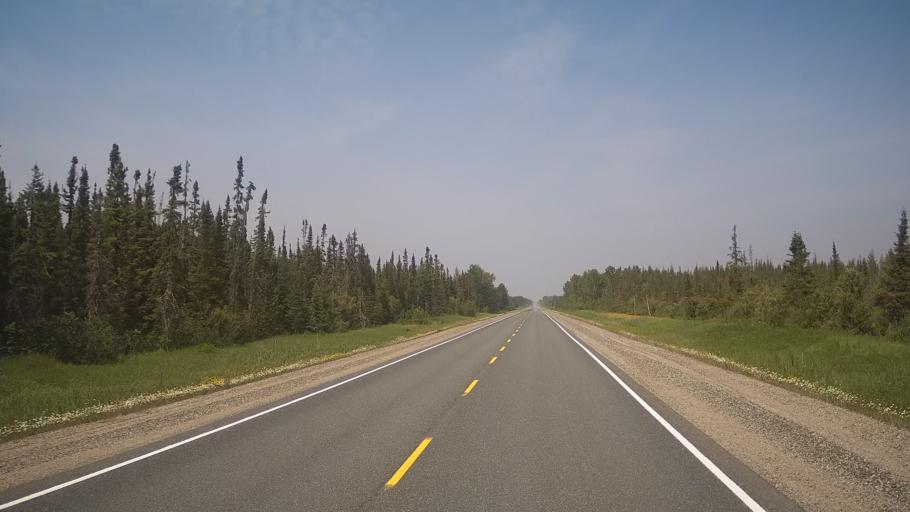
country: CA
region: Ontario
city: Timmins
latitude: 48.7961
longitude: -81.3667
